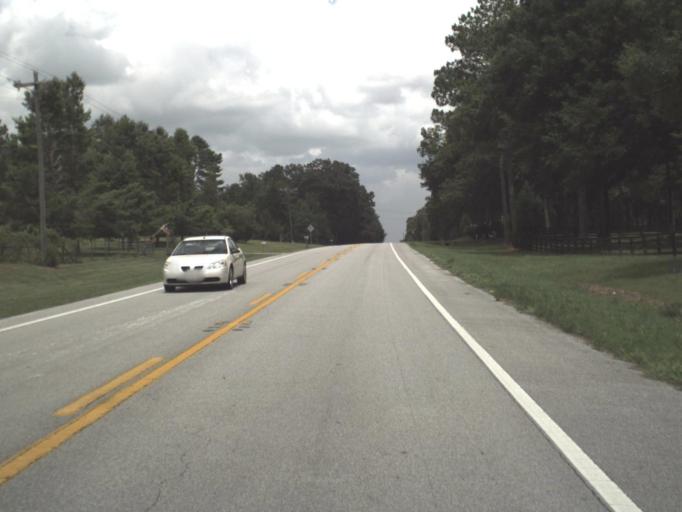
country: US
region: Florida
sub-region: Madison County
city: Madison
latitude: 30.4723
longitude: -83.3580
